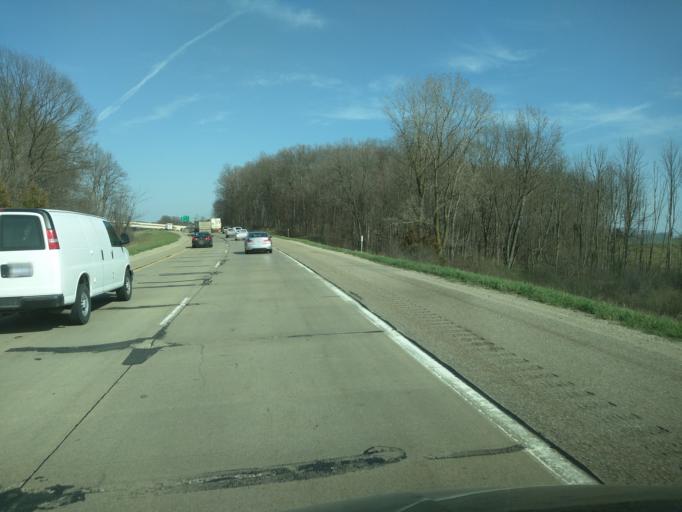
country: US
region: Michigan
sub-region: Kent County
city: Forest Hills
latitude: 42.8896
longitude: -85.5011
